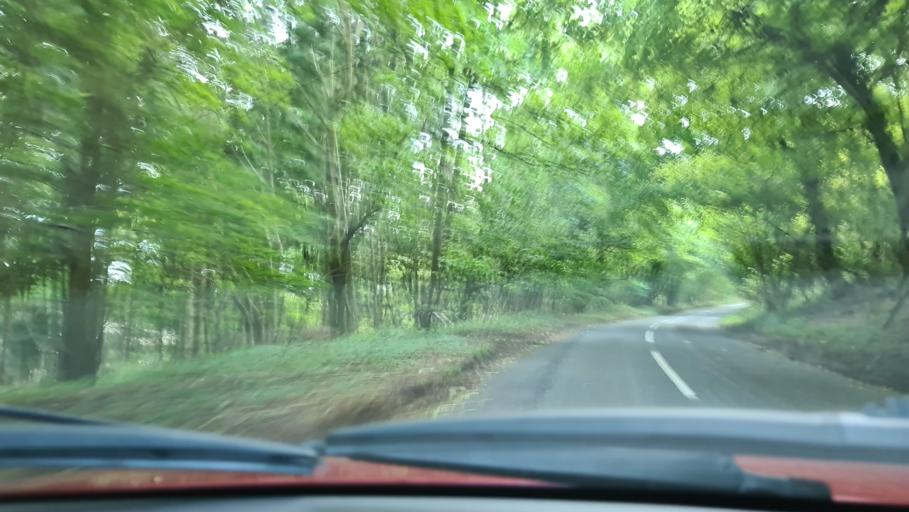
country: GB
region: England
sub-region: Buckinghamshire
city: Princes Risborough
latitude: 51.7318
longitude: -0.7846
